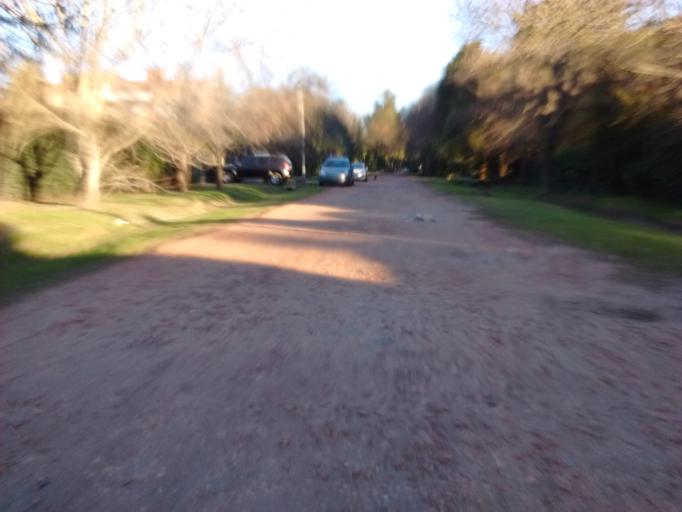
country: AR
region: Santa Fe
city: Funes
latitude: -32.9145
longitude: -60.8329
